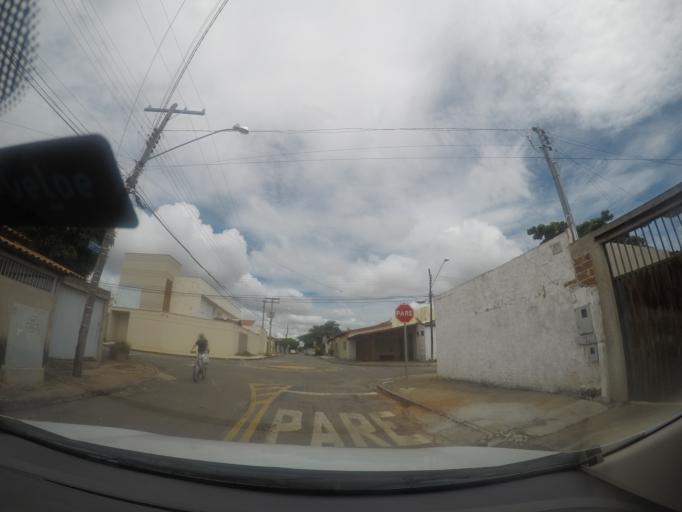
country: BR
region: Goias
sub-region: Goiania
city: Goiania
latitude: -16.6591
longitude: -49.2982
